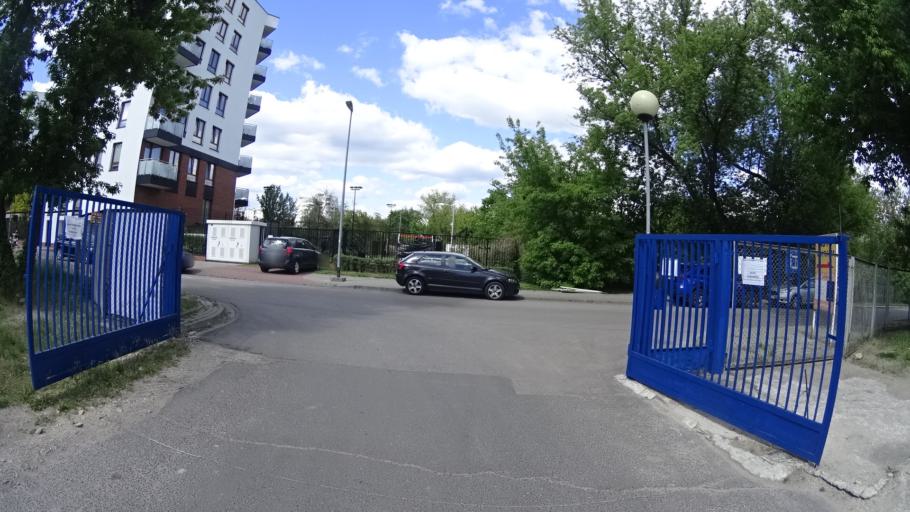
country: PL
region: Masovian Voivodeship
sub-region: Warszawa
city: Bemowo
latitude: 52.2721
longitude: 20.9149
